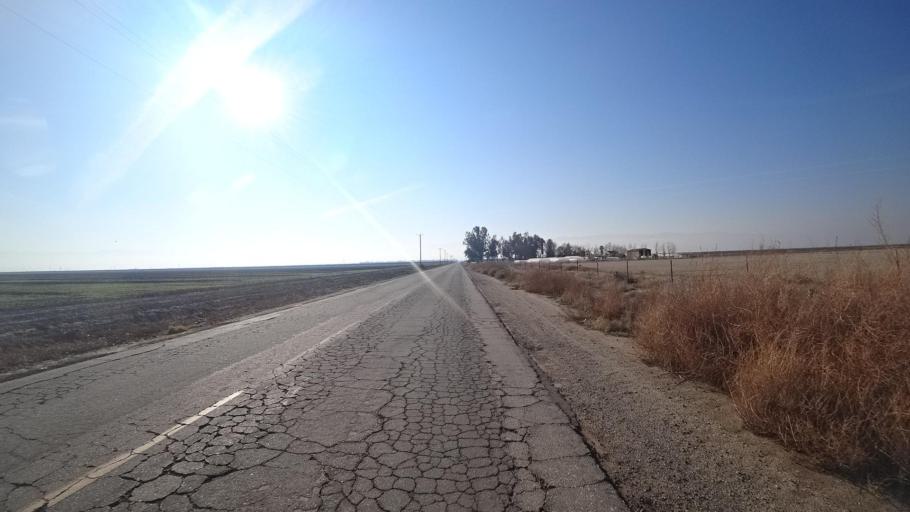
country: US
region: California
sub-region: Kern County
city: Weedpatch
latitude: 35.1558
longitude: -118.9677
